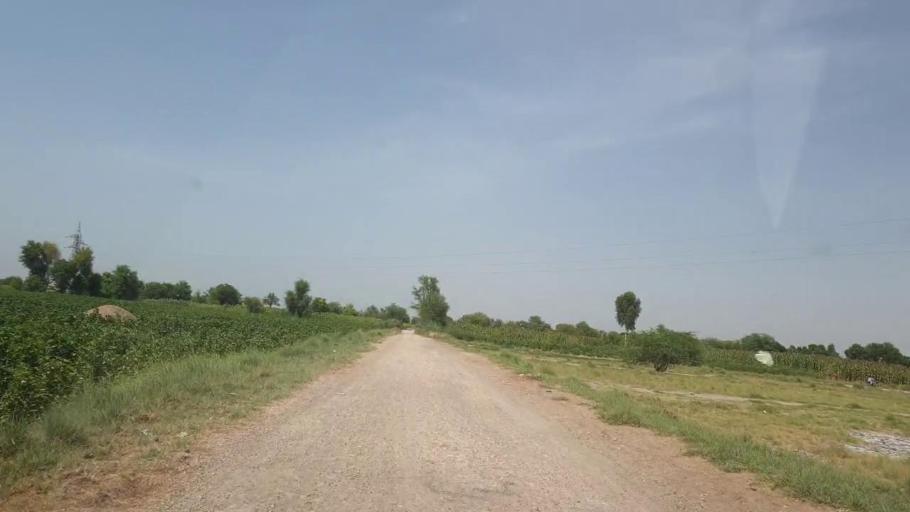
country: PK
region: Sindh
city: Bozdar
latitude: 27.0859
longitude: 68.6016
